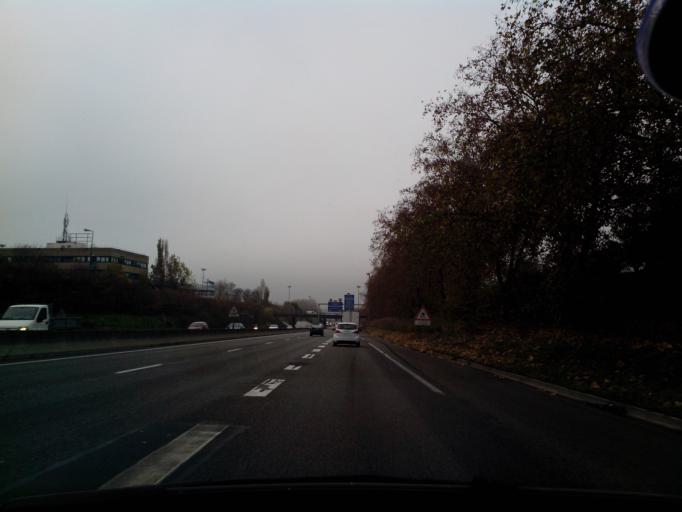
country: FR
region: Ile-de-France
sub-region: Departement de l'Essonne
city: Wissous
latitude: 48.7312
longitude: 2.3152
